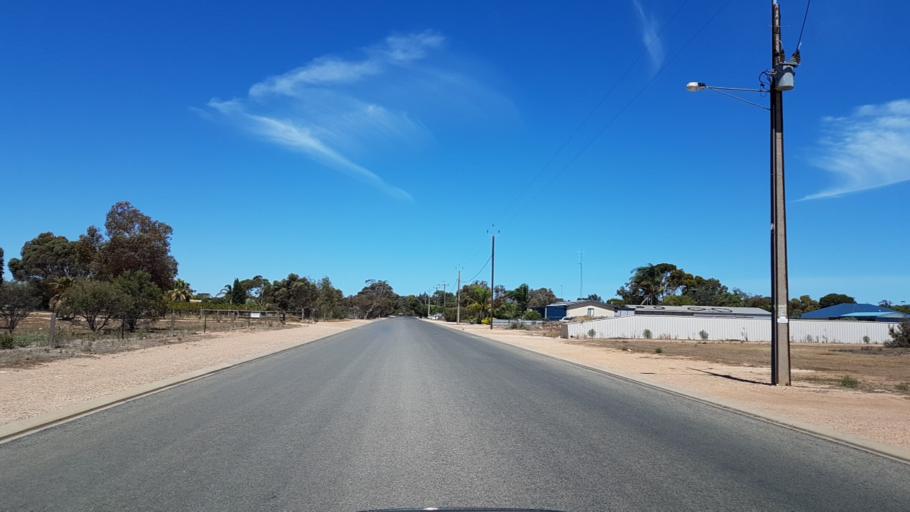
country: AU
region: South Australia
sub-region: Copper Coast
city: Wallaroo
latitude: -34.0571
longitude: 137.5821
